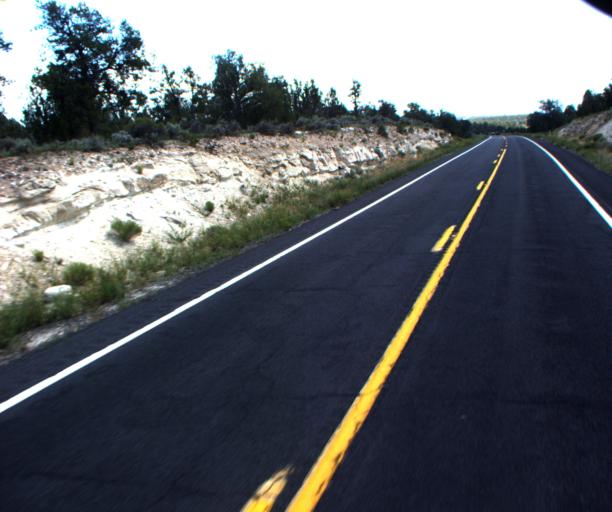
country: US
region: Arizona
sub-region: Coconino County
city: Grand Canyon Village
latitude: 35.8569
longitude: -112.1337
